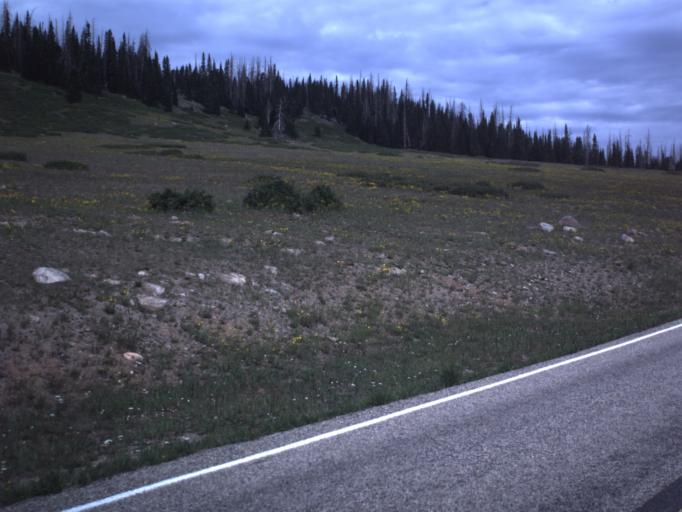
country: US
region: Utah
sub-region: Iron County
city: Cedar City
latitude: 37.6015
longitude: -112.8505
